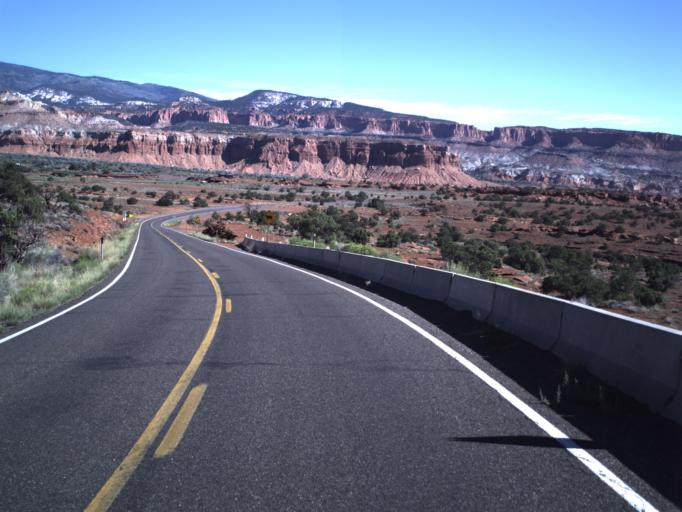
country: US
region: Utah
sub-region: Wayne County
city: Loa
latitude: 38.3006
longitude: -111.3916
